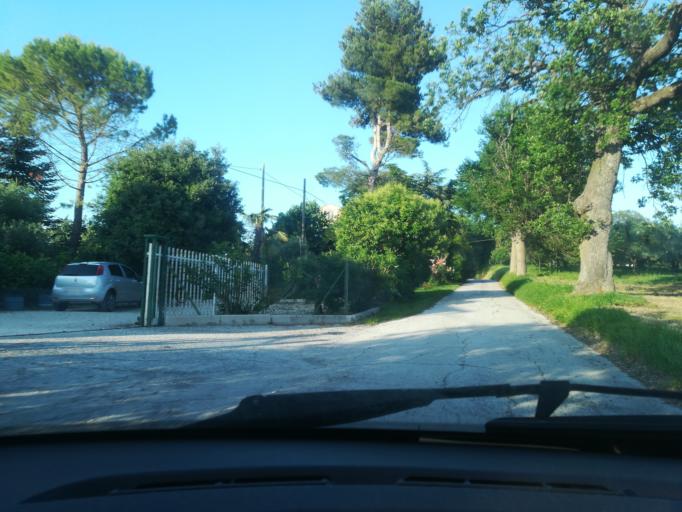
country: IT
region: The Marches
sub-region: Provincia di Macerata
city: Macerata
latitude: 43.2828
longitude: 13.4629
